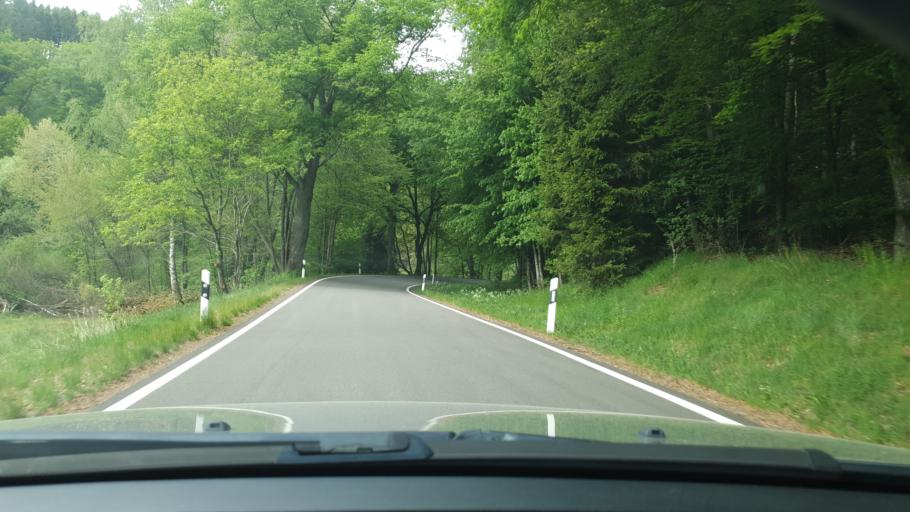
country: DE
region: Rheinland-Pfalz
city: Gerhardsbrunn
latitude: 49.3469
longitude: 7.5353
